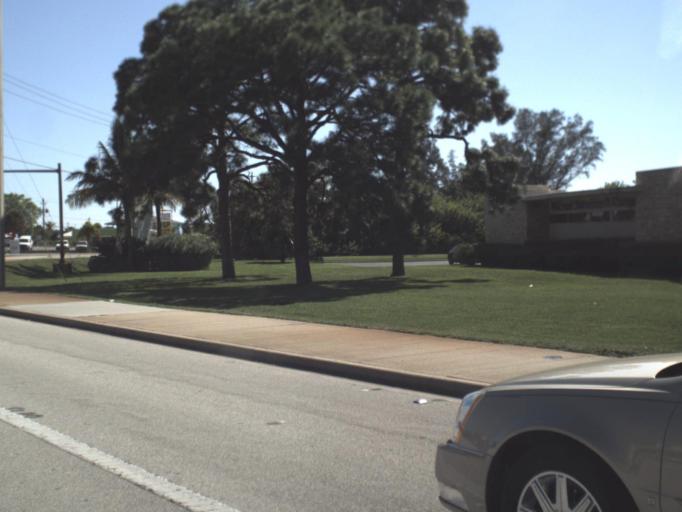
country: US
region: Florida
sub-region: Charlotte County
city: Manasota Key
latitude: 26.9416
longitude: -82.3495
